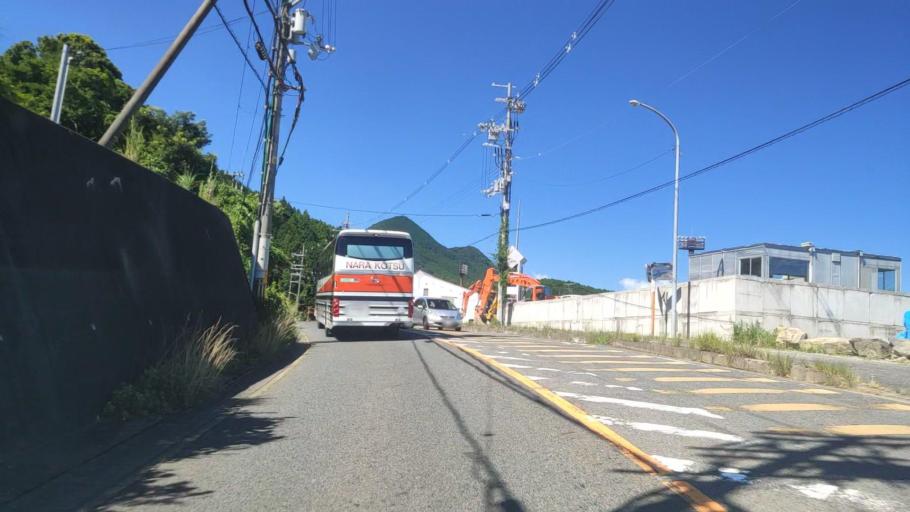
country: JP
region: Nara
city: Haibara-akanedai
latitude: 34.5401
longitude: 135.9558
